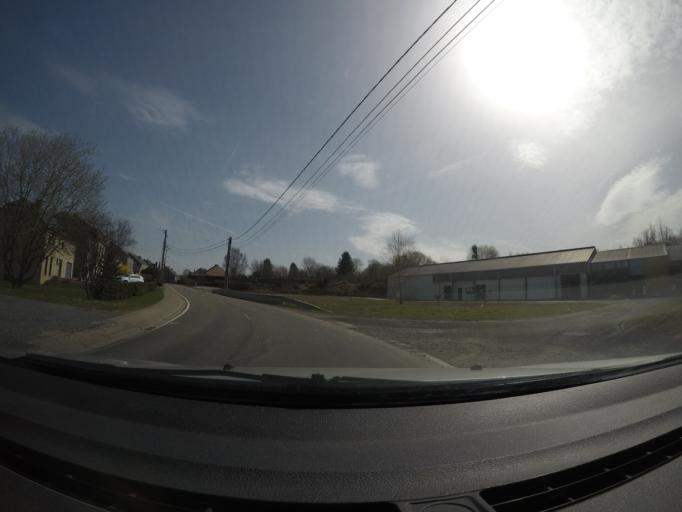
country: BE
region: Wallonia
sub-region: Province du Luxembourg
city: Habay-la-Vieille
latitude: 49.7178
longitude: 5.5792
